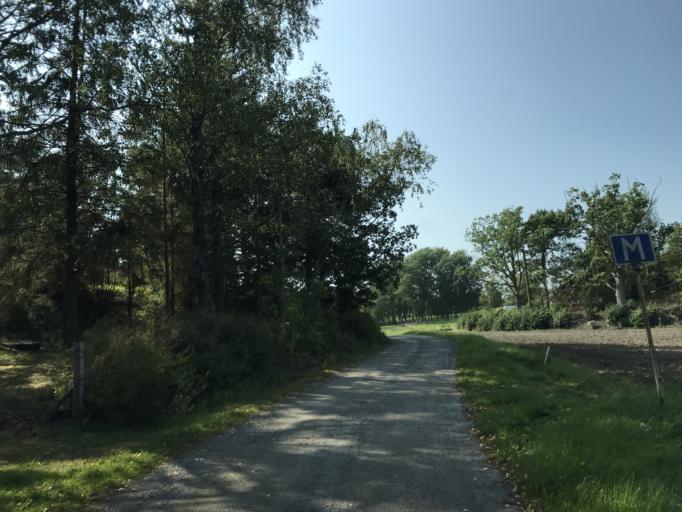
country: SE
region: Stockholm
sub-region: Norrtalje Kommun
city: Bjorko
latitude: 59.8474
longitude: 19.0174
